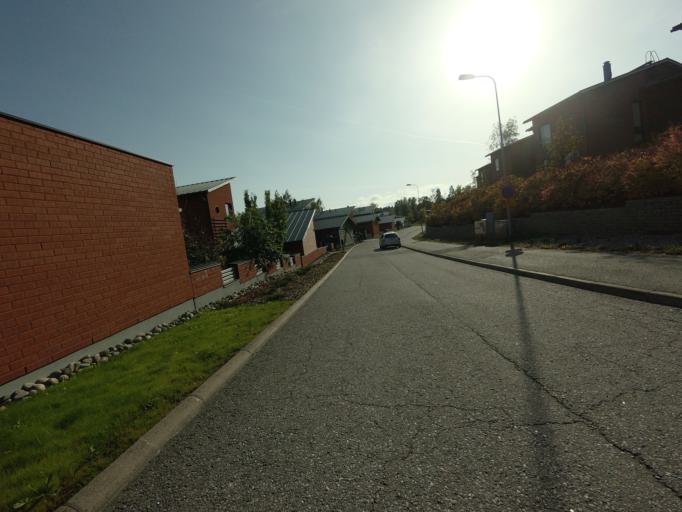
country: FI
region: Uusimaa
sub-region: Helsinki
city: Espoo
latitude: 60.1727
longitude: 24.6441
